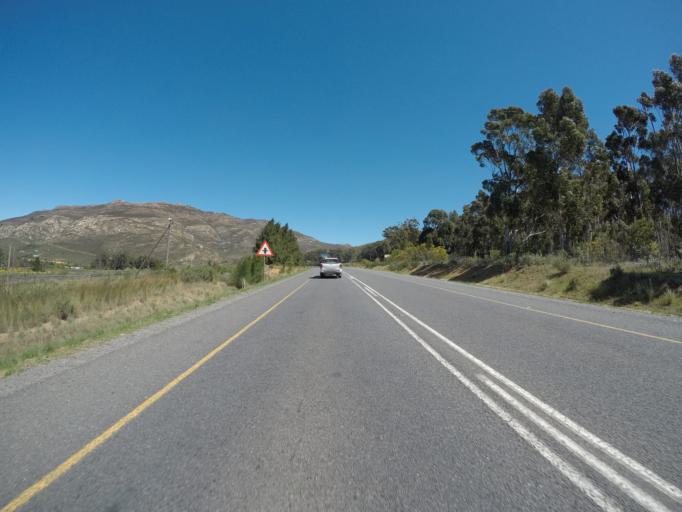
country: ZA
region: Western Cape
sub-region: Cape Winelands District Municipality
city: Ceres
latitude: -33.3120
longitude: 19.0969
